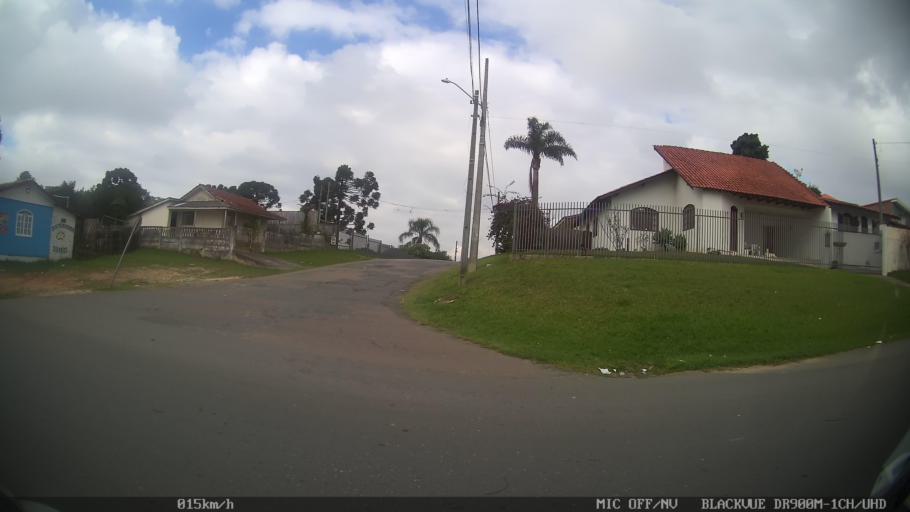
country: BR
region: Parana
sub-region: Almirante Tamandare
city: Almirante Tamandare
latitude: -25.3540
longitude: -49.2583
